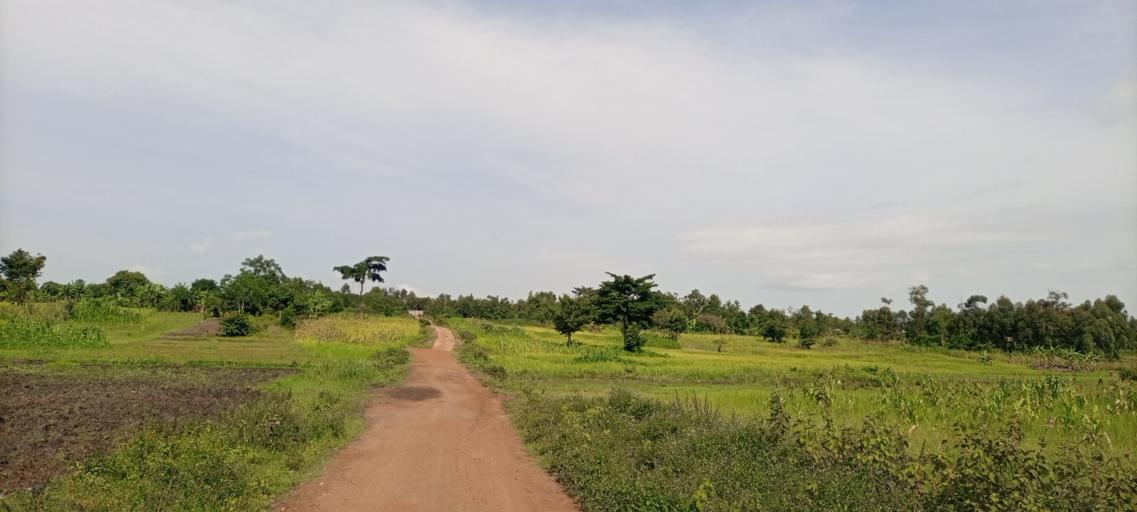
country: UG
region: Eastern Region
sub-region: Mbale District
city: Mbale
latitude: 1.1280
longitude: 34.0346
